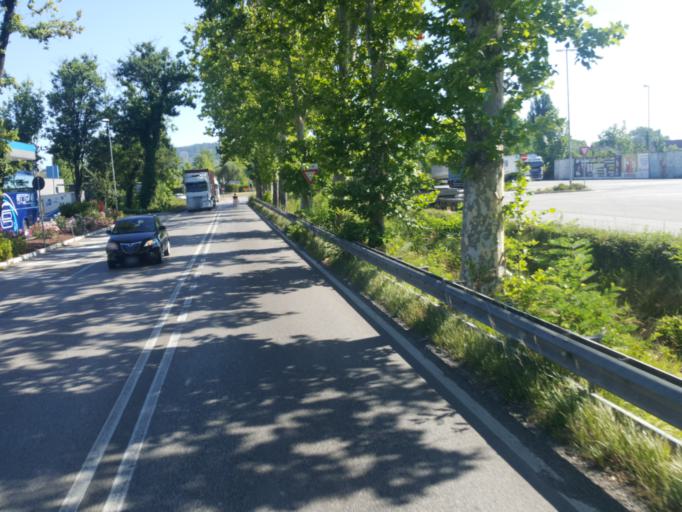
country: IT
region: The Marches
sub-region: Provincia di Pesaro e Urbino
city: Villa Ceccolini
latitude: 43.8897
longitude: 12.8325
